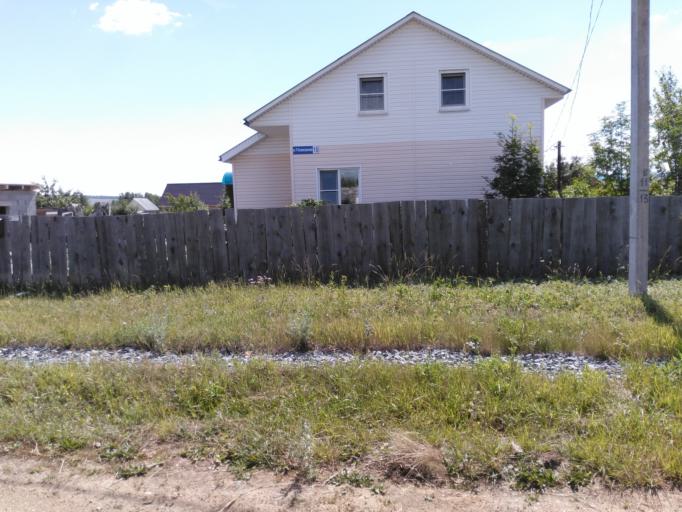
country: RU
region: Bashkortostan
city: Uchaly
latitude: 54.2893
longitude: 59.3639
